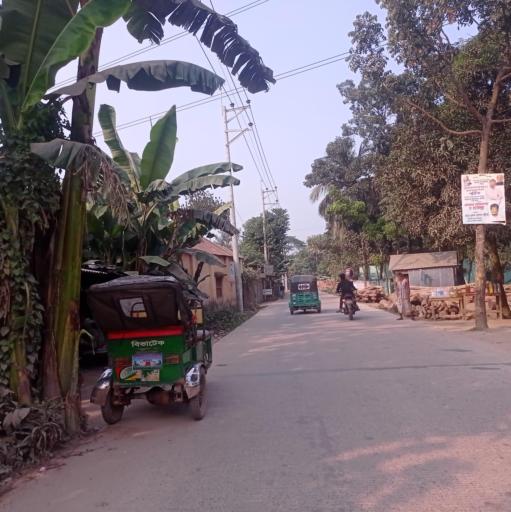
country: BD
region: Dhaka
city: Bhairab Bazar
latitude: 24.0981
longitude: 90.8528
